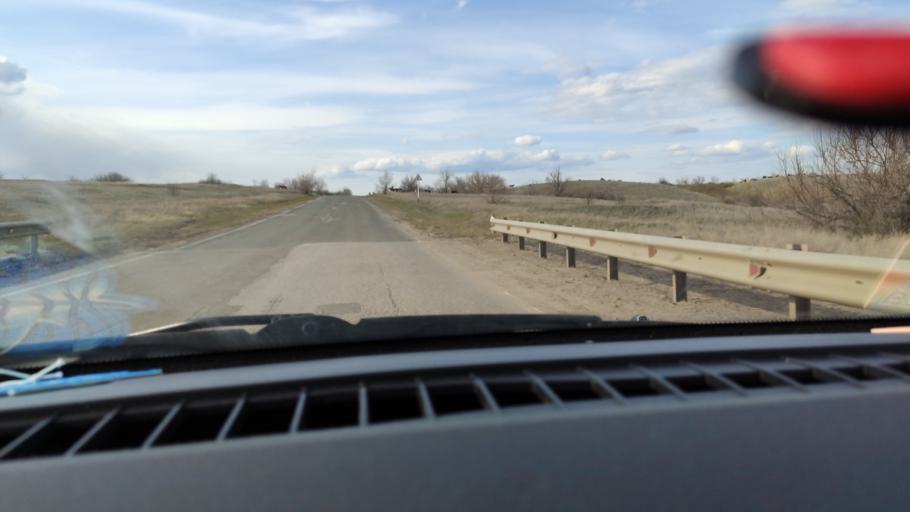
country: RU
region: Saratov
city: Rovnoye
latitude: 50.9644
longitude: 46.1169
